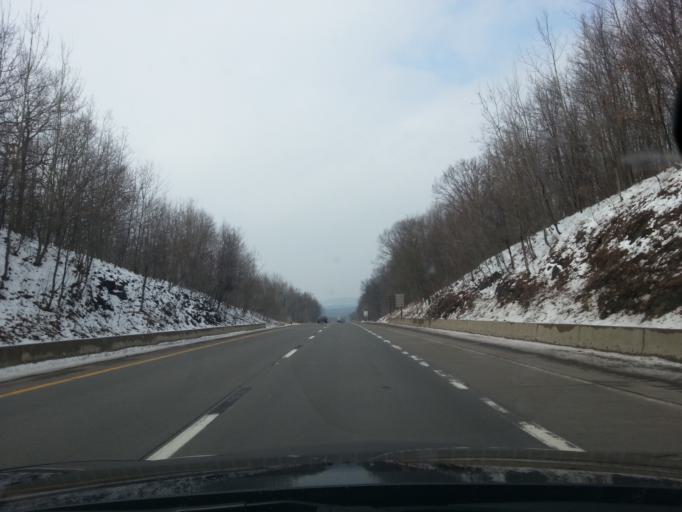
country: US
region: Pennsylvania
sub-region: Luzerne County
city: Freeland
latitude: 41.0886
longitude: -75.9623
